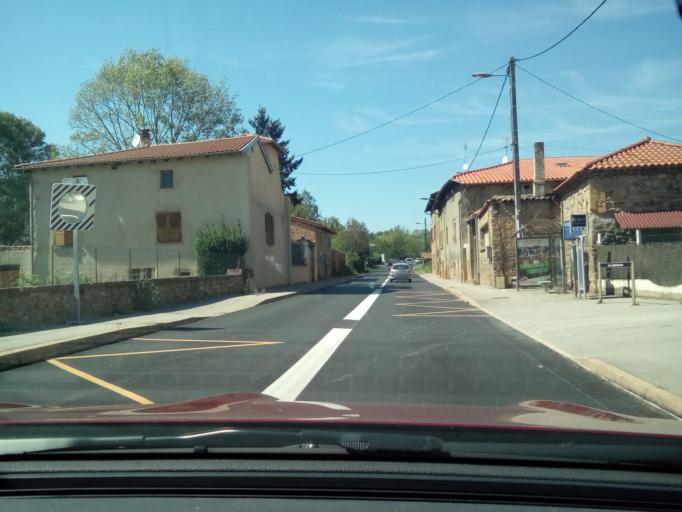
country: FR
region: Rhone-Alpes
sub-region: Departement du Rhone
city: Chatillon
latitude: 45.8967
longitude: 4.5912
